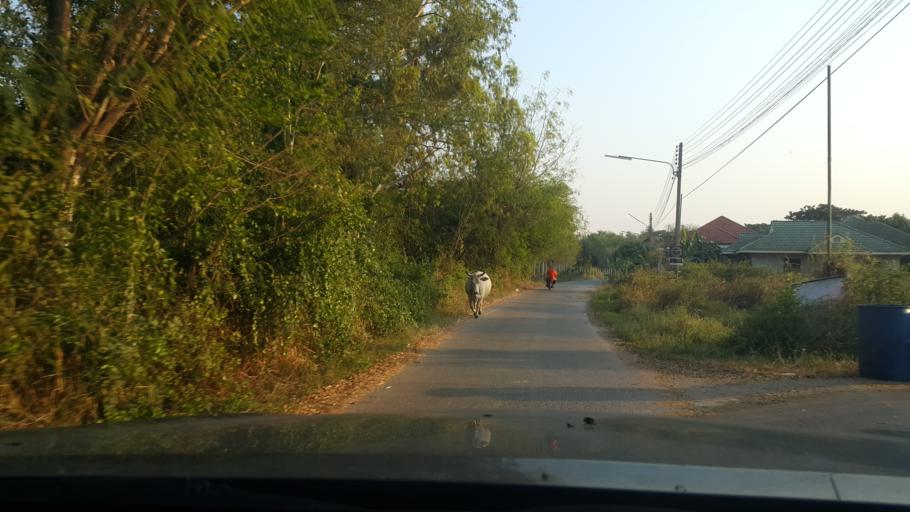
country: TH
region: Nakhon Ratchasima
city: Nakhon Ratchasima
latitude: 14.9488
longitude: 102.0311
